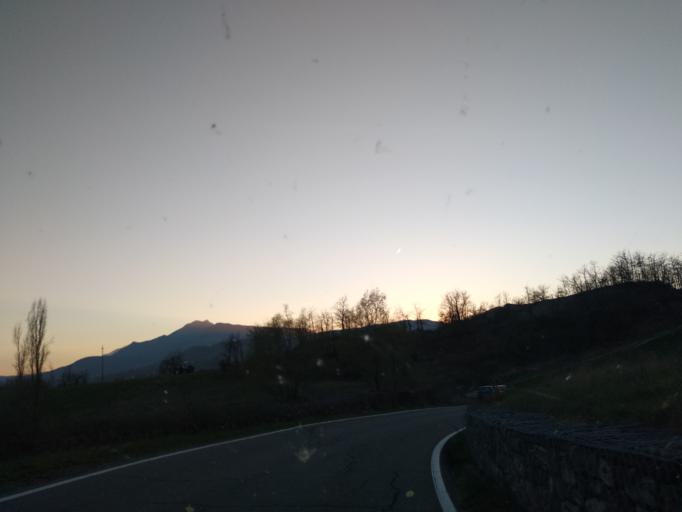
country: IT
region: Emilia-Romagna
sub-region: Provincia di Reggio Emilia
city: Castelnovo ne'Monti
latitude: 44.4117
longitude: 10.3995
